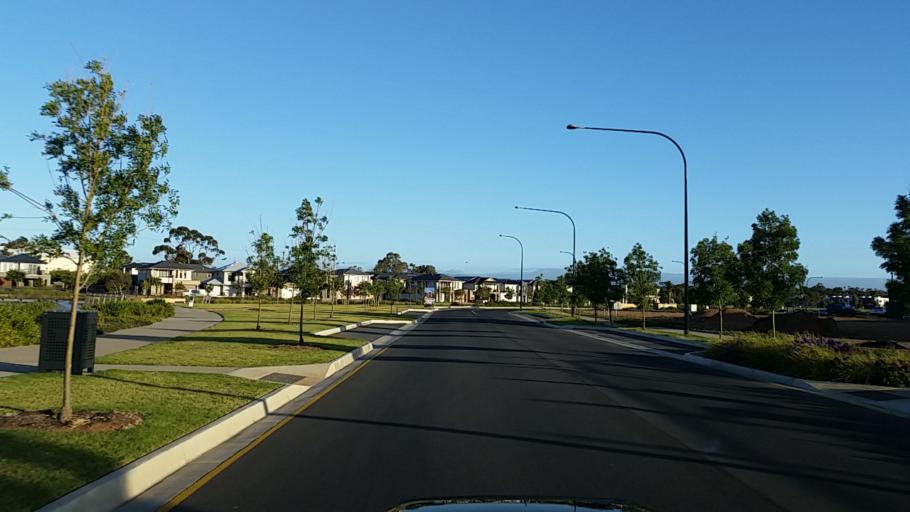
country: AU
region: South Australia
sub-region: Charles Sturt
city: Woodville North
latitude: -34.8698
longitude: 138.5335
